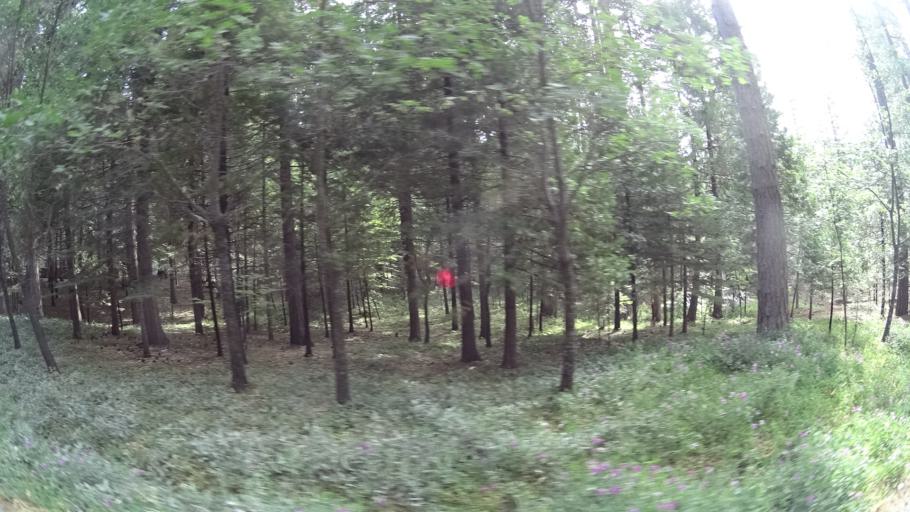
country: US
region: California
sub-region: Calaveras County
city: Arnold
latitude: 38.2520
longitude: -120.3346
